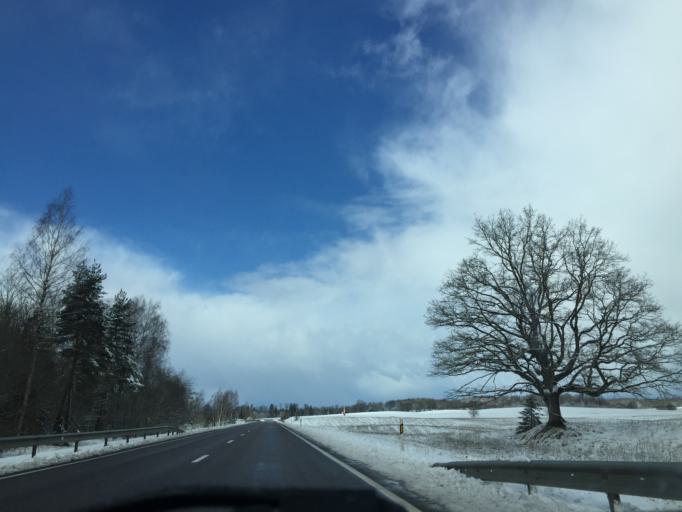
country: LV
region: Talsu Rajons
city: Talsi
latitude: 57.1887
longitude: 22.6054
